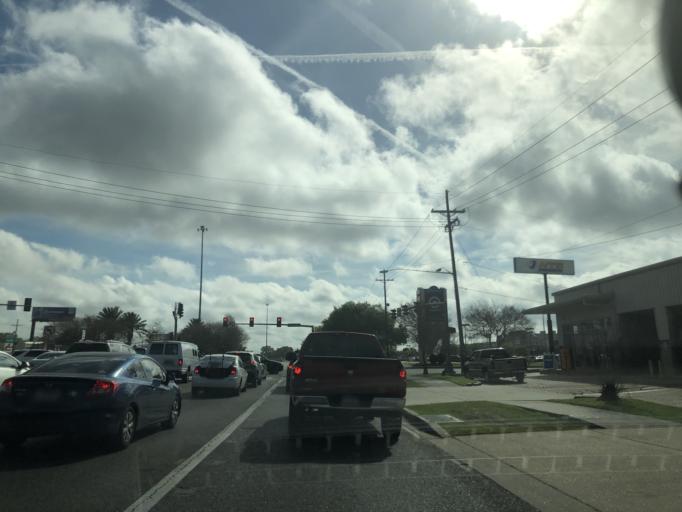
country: US
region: Louisiana
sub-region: Jefferson Parish
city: Metairie Terrace
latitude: 30.0050
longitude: -90.1862
